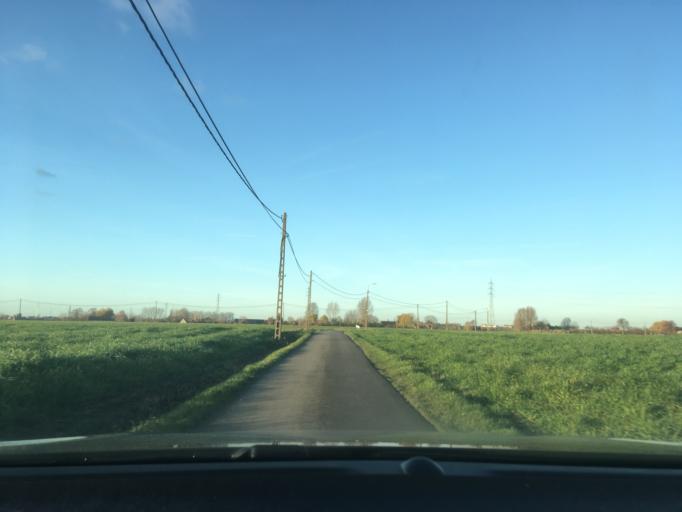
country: BE
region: Flanders
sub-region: Provincie West-Vlaanderen
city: Menen
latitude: 50.8240
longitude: 3.1045
